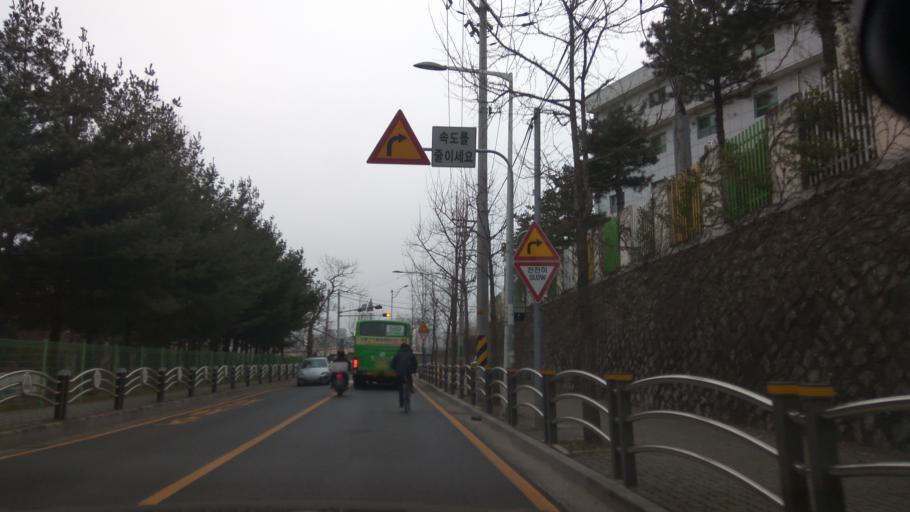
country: KR
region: Incheon
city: Incheon
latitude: 37.4941
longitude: 126.7091
